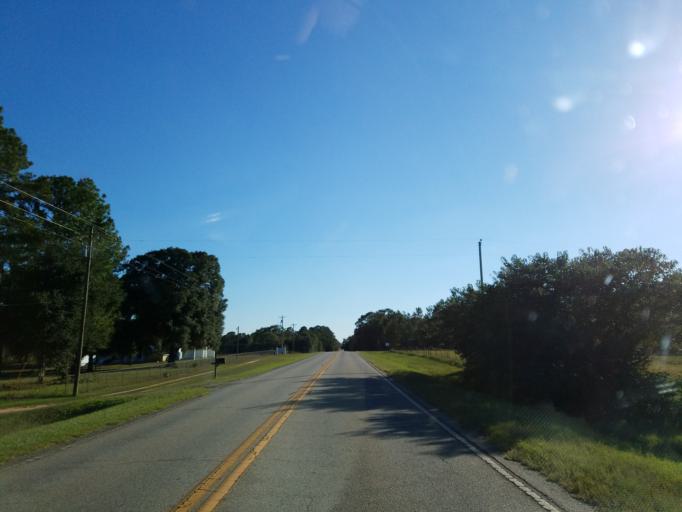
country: US
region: Georgia
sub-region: Lee County
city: Leesburg
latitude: 31.7691
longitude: -84.1441
